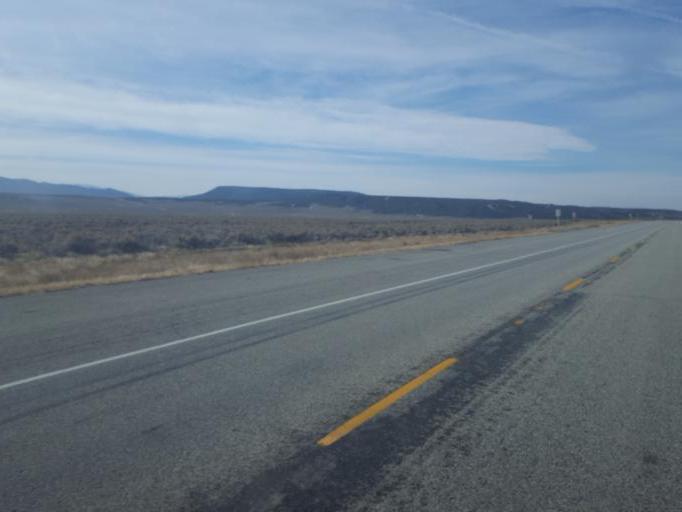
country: US
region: Colorado
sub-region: Costilla County
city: San Luis
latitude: 37.4517
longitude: -105.3697
